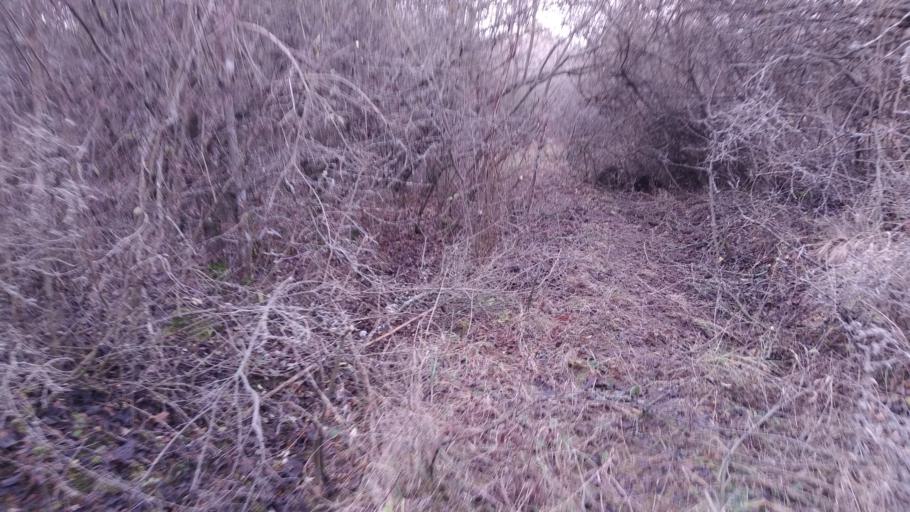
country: HU
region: Pest
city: Pomaz
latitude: 47.6223
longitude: 19.0168
